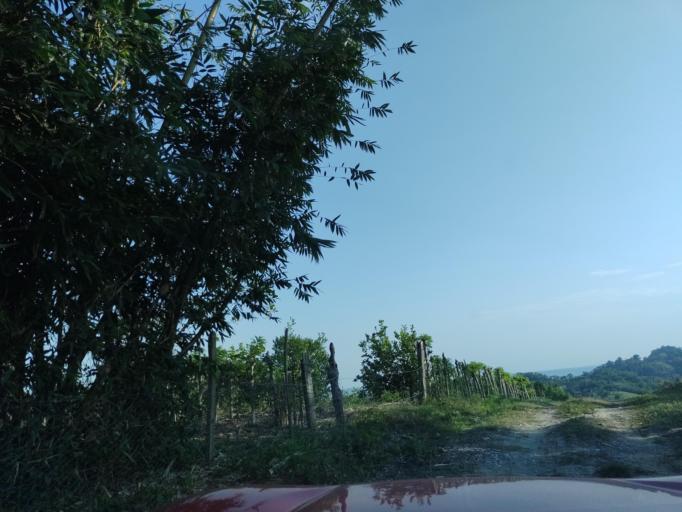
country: MX
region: Veracruz
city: Agua Dulce
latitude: 20.2823
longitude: -97.2502
